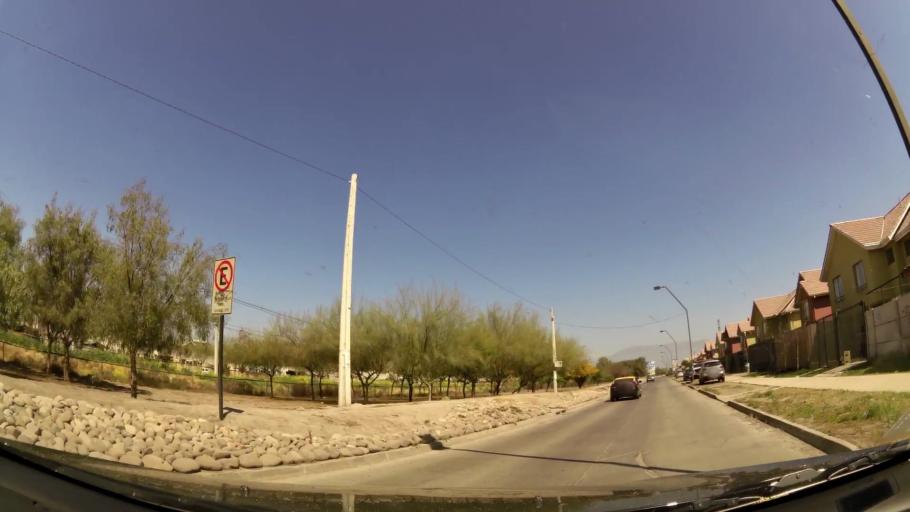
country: CL
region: Santiago Metropolitan
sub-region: Provincia de Chacabuco
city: Chicureo Abajo
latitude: -33.3257
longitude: -70.7511
